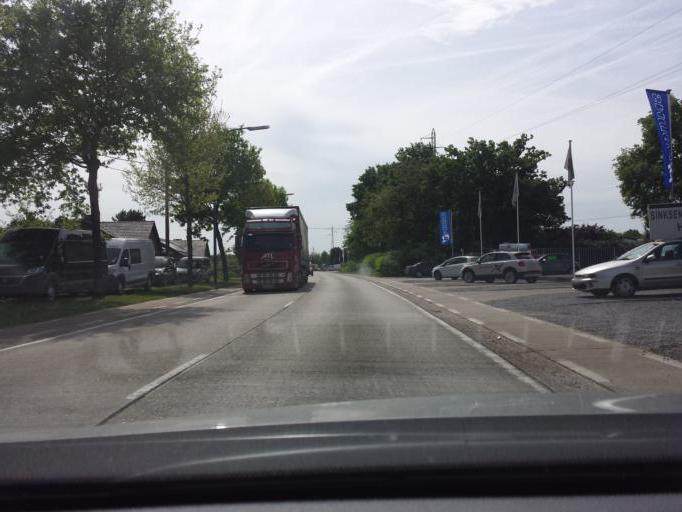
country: BE
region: Flanders
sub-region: Provincie Limburg
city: Beringen
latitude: 51.0466
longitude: 5.1878
